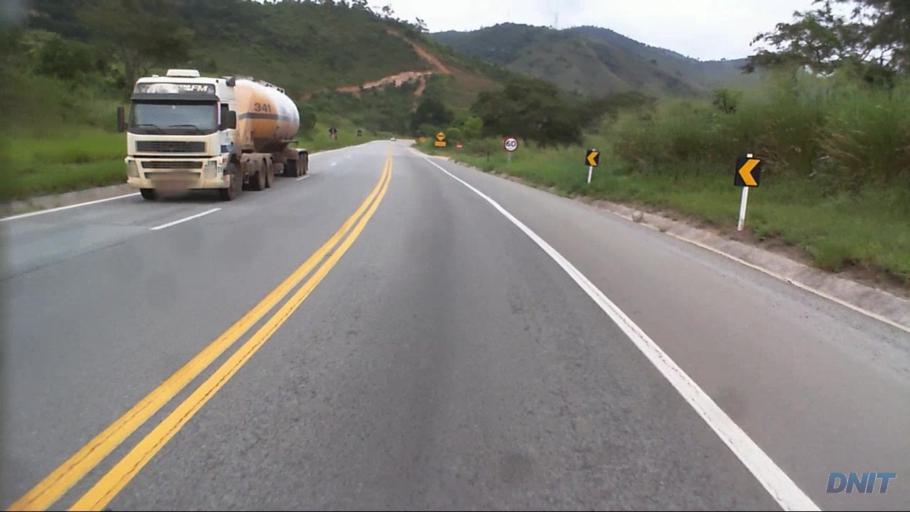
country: BR
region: Minas Gerais
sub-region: Nova Era
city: Nova Era
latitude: -19.6398
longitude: -42.9163
